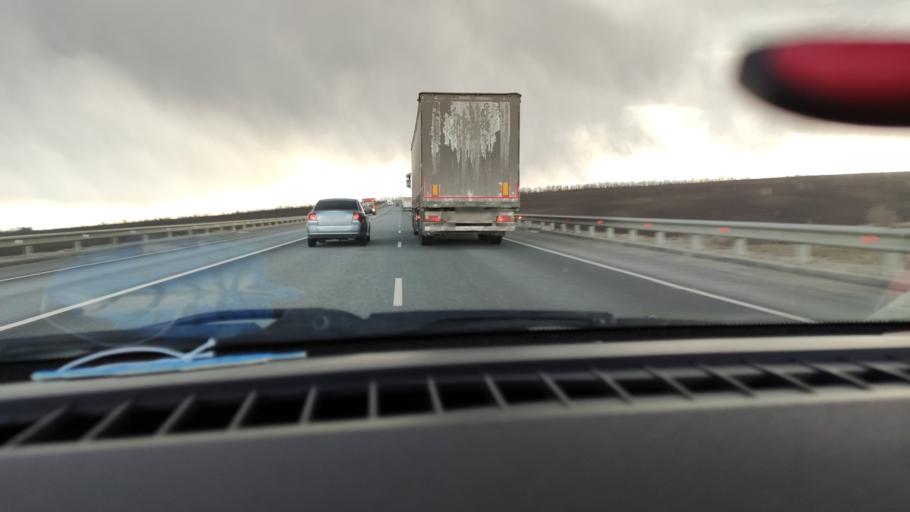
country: RU
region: Saratov
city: Yelshanka
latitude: 51.8391
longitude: 46.4759
